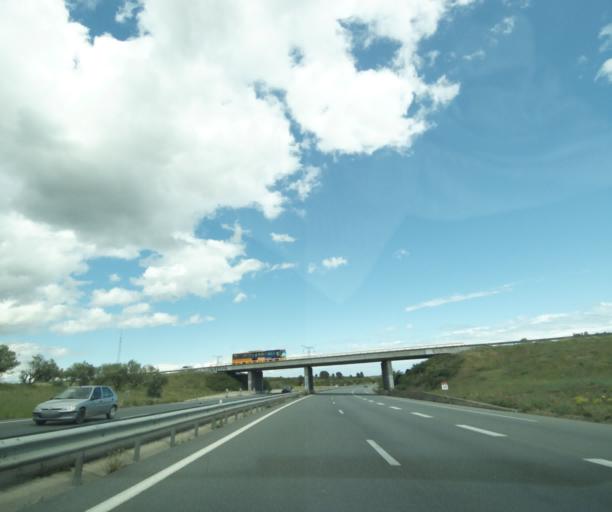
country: FR
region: Languedoc-Roussillon
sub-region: Departement de l'Herault
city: Murviel-les-Montpellier
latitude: 43.6339
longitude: 3.7557
